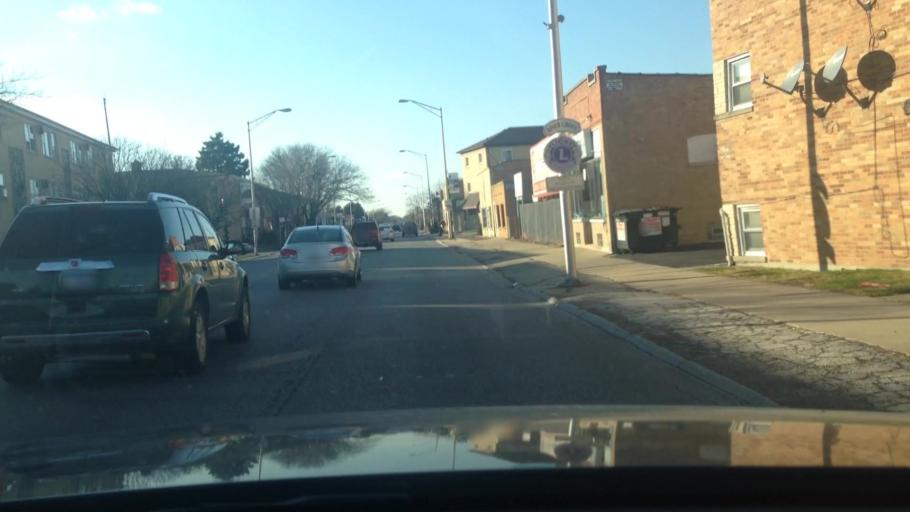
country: US
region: Illinois
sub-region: Cook County
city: River Grove
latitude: 41.9274
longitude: -87.8274
